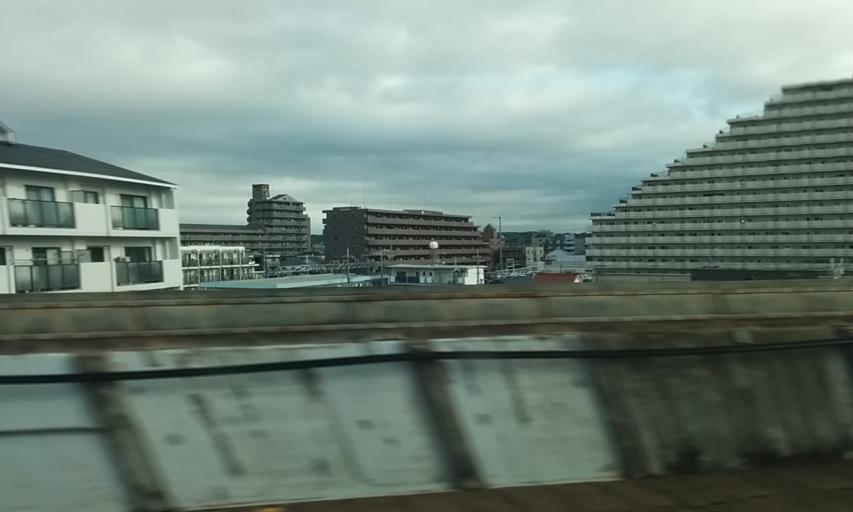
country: JP
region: Hyogo
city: Akashi
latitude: 34.6673
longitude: 134.9565
